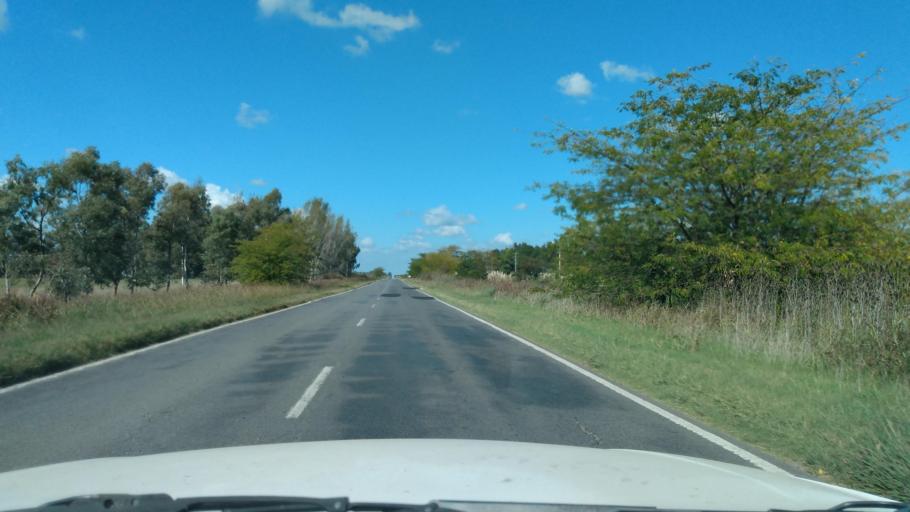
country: AR
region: Buenos Aires
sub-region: Partido de Mercedes
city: Mercedes
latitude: -34.7170
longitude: -59.3963
